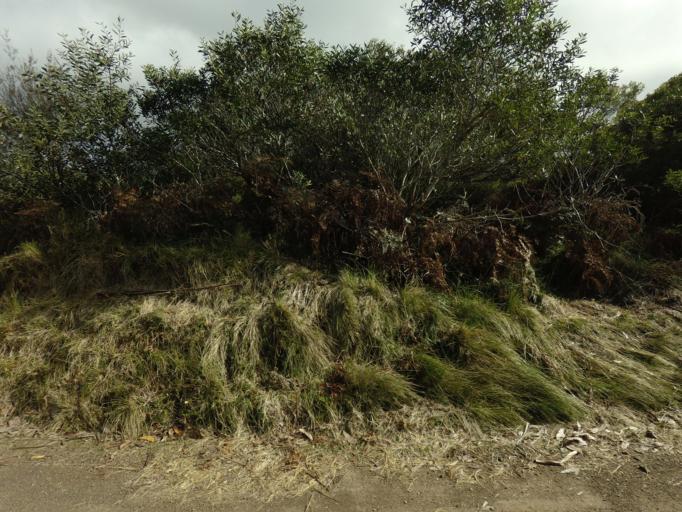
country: AU
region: Tasmania
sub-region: Huon Valley
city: Geeveston
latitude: -43.5791
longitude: 146.9007
